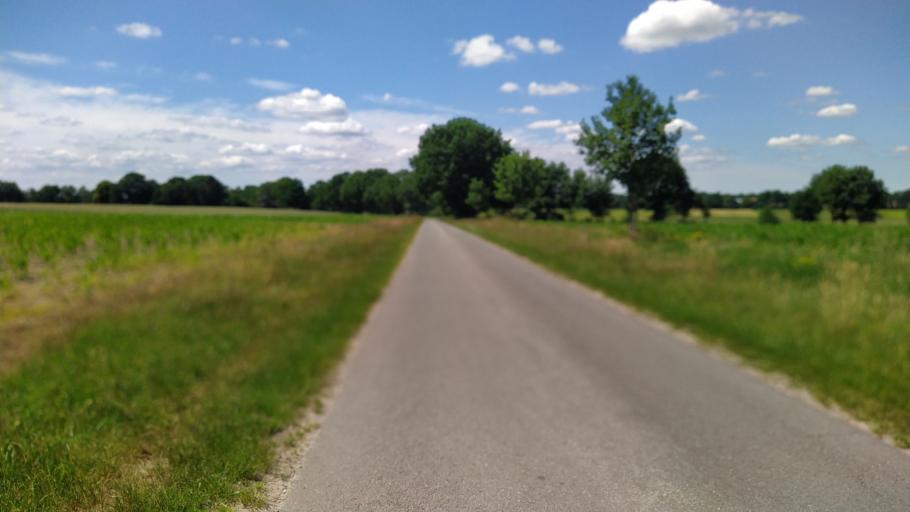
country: DE
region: Lower Saxony
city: Estorf
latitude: 53.5618
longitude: 9.2202
